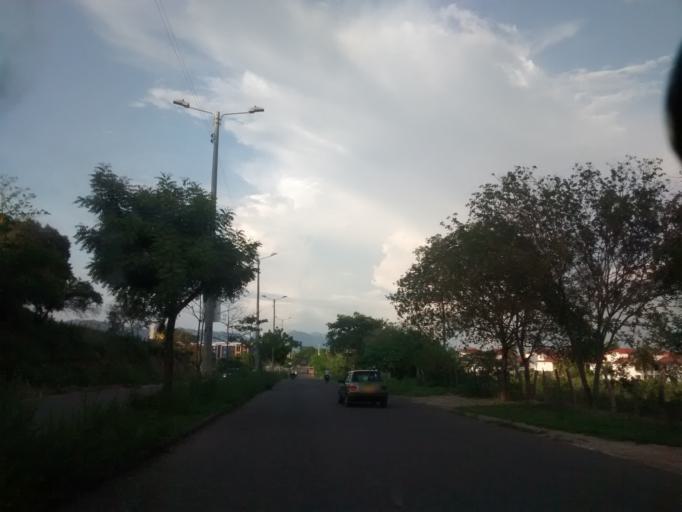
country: CO
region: Cundinamarca
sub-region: Girardot
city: Girardot City
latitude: 4.3178
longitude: -74.8071
